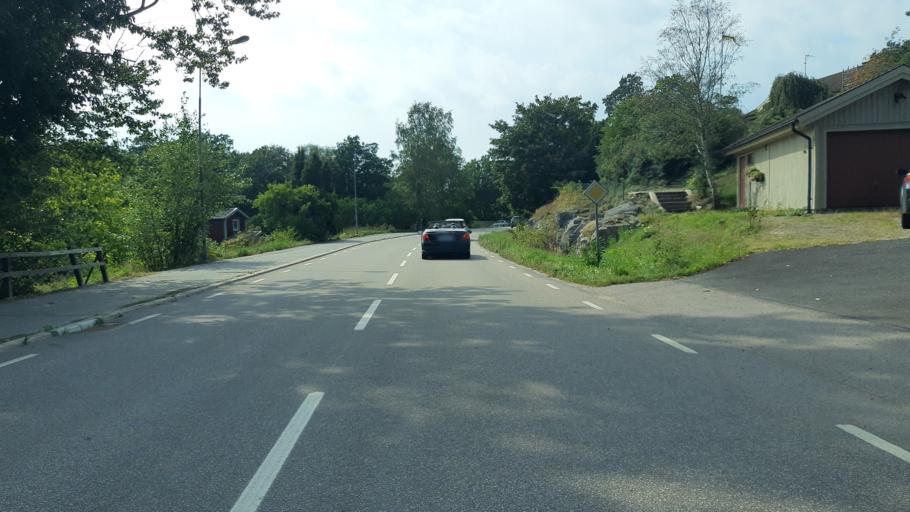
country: SE
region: Blekinge
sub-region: Karlskrona Kommun
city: Nattraby
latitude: 56.1930
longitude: 15.5335
